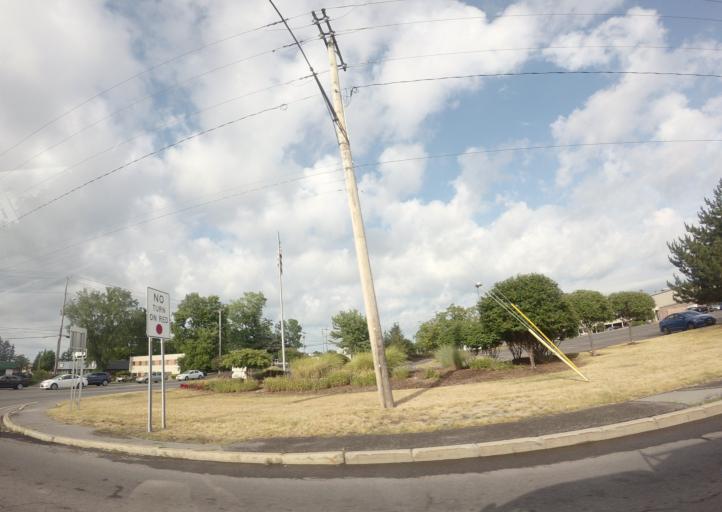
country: US
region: New York
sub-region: Onondaga County
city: East Syracuse
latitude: 43.0424
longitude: -76.0675
